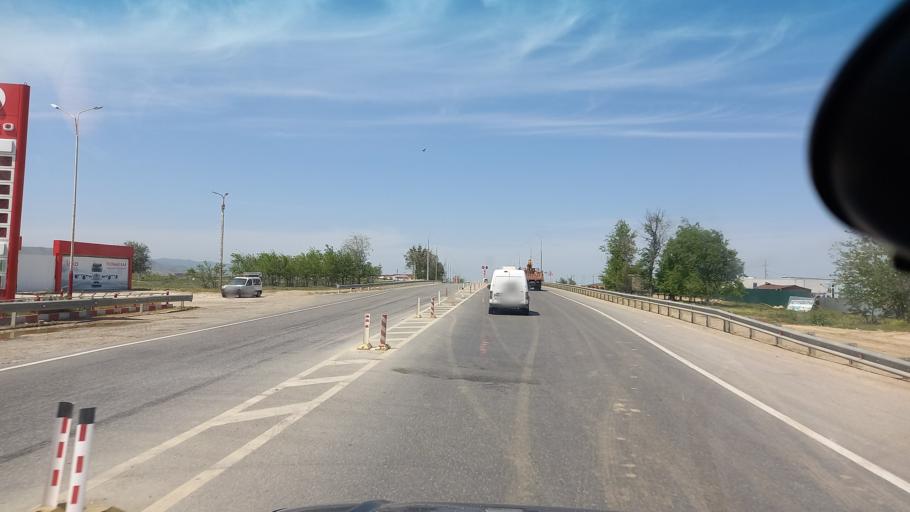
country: RU
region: Dagestan
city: Manas
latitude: 42.7277
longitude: 47.6662
